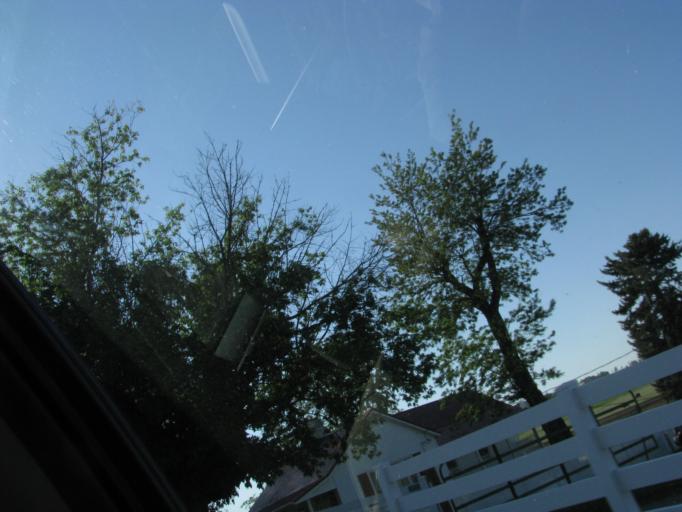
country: US
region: Washington
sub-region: Spokane County
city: Liberty Lake
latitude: 47.6277
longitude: -117.1486
